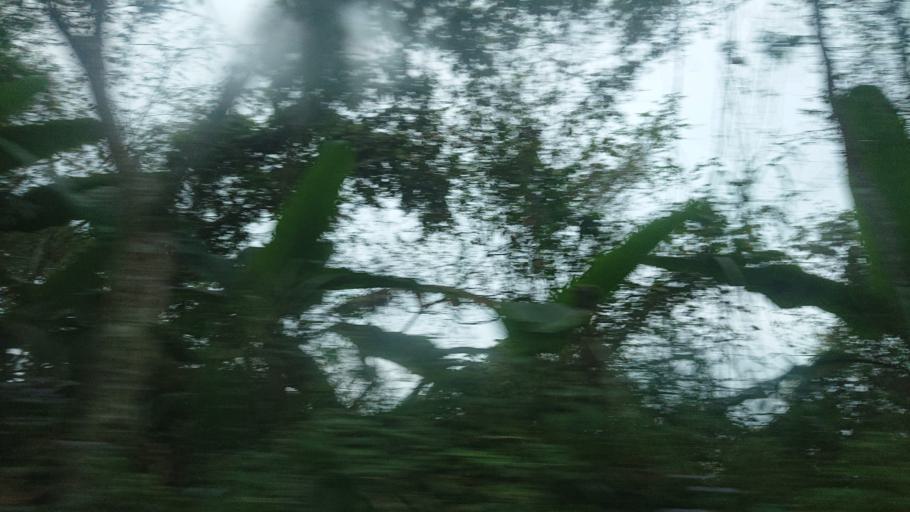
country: TW
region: Taiwan
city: Lugu
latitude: 23.5955
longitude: 120.7145
